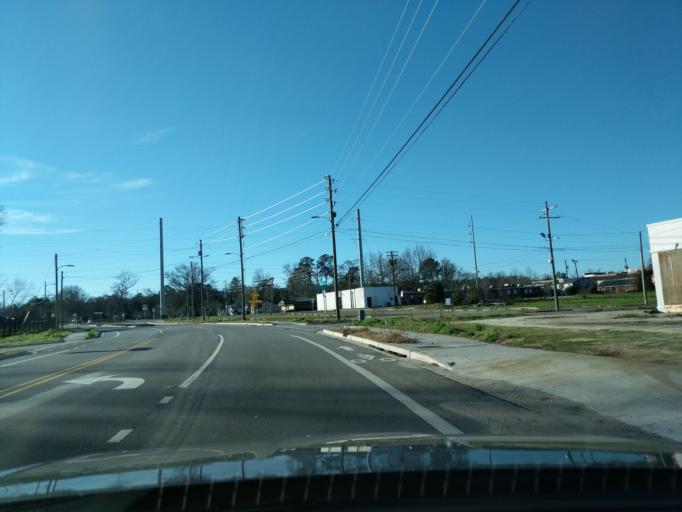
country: US
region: Georgia
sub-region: Richmond County
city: Augusta
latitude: 33.4714
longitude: -81.9949
